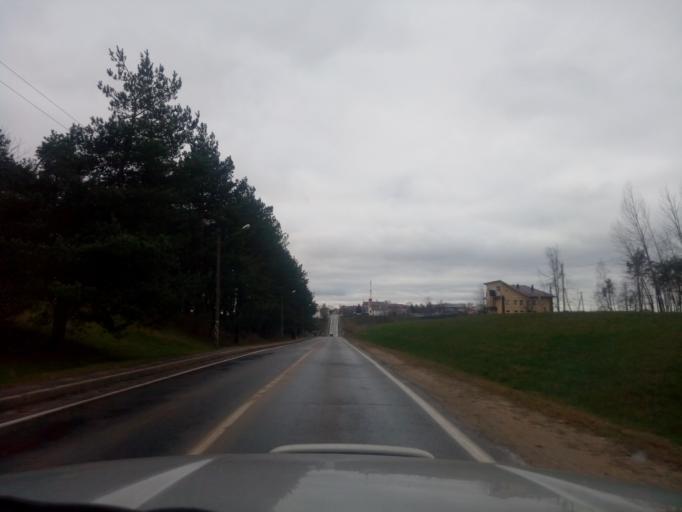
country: BY
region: Minsk
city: Kapyl'
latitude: 53.1551
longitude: 27.0998
